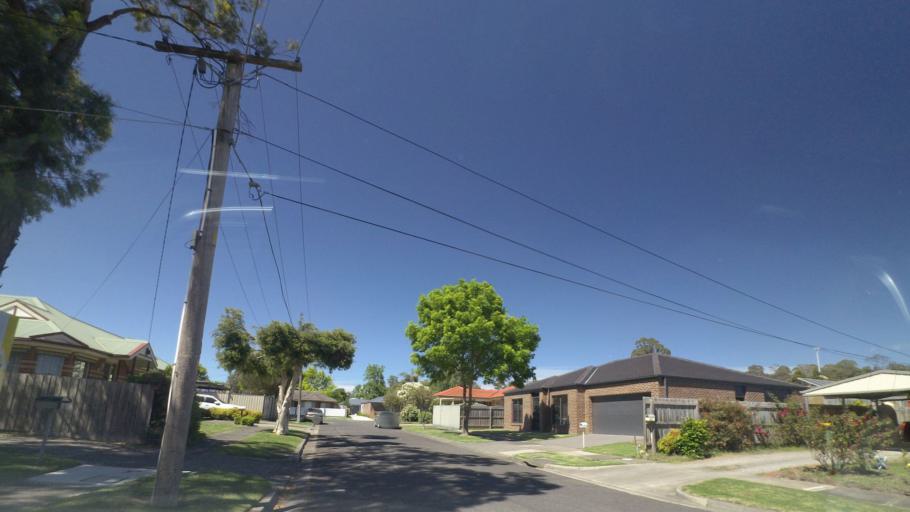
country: AU
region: Victoria
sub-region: Yarra Ranges
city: Kilsyth
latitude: -37.7982
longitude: 145.3179
